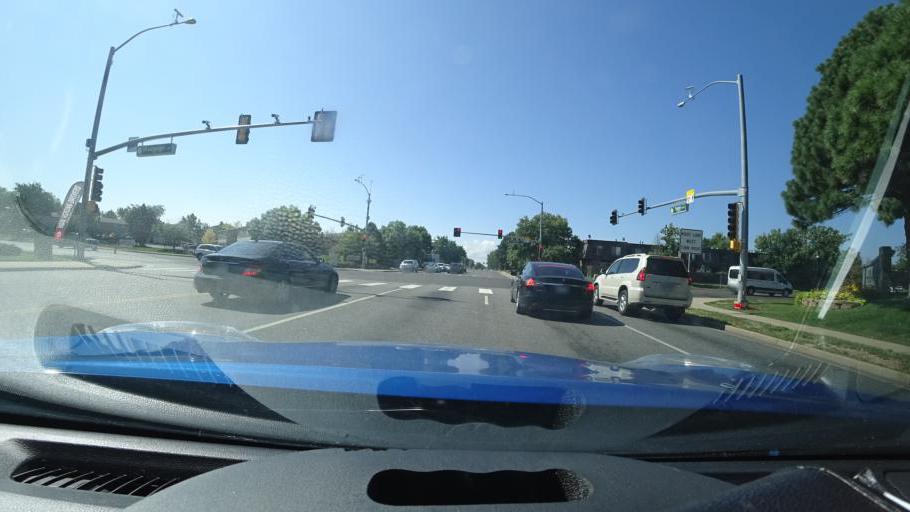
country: US
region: Colorado
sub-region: Adams County
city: Aurora
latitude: 39.6969
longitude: -104.8193
